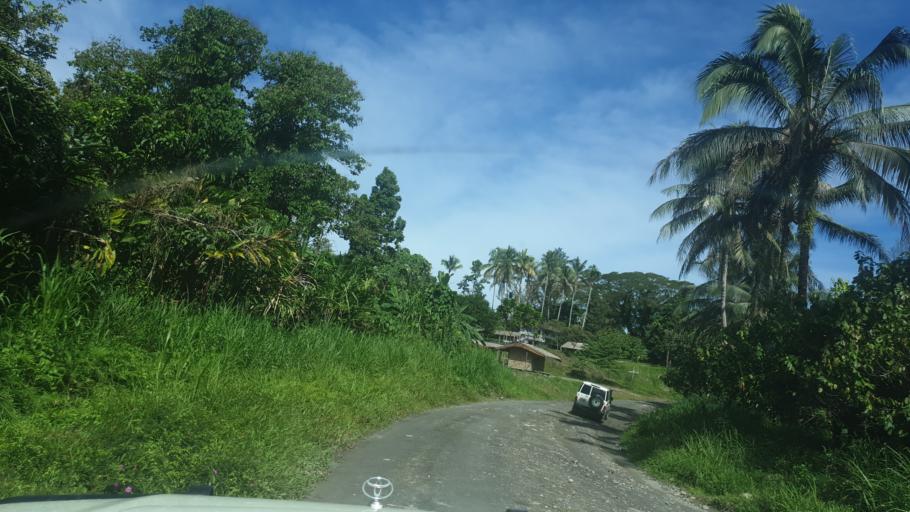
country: PG
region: Bougainville
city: Panguna
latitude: -6.5021
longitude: 155.3296
